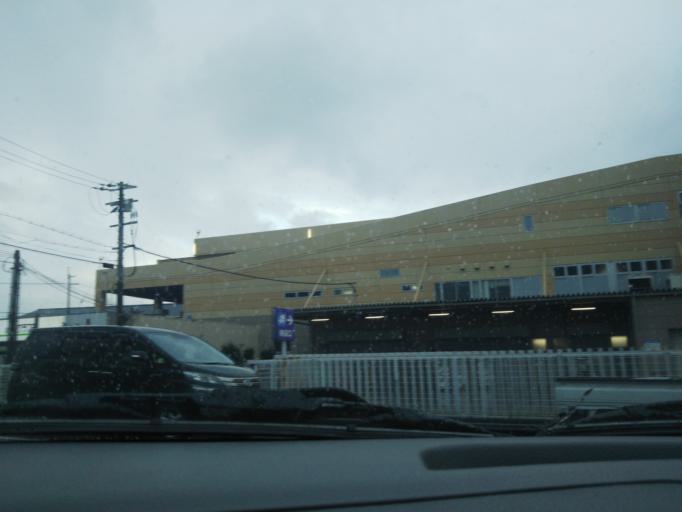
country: JP
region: Shiga Prefecture
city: Minakuchicho-matoba
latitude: 34.9652
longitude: 136.1685
